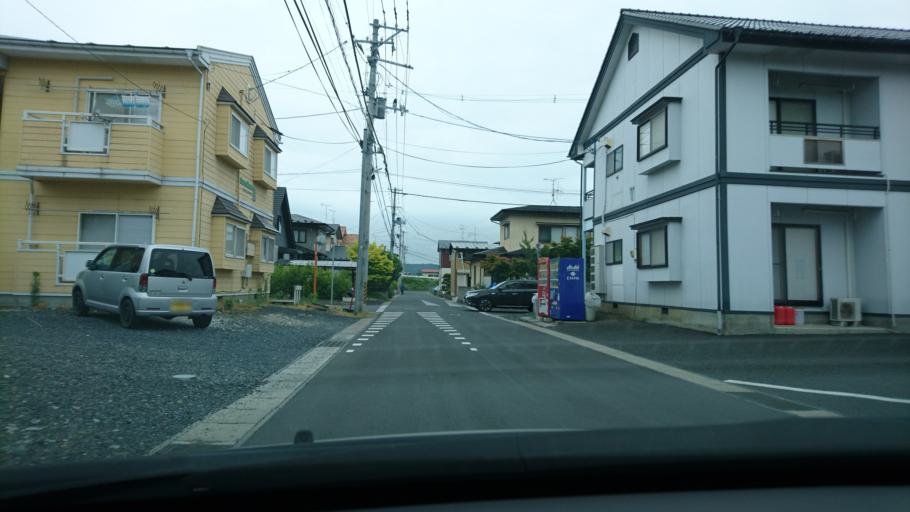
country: JP
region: Iwate
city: Ichinoseki
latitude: 38.9169
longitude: 141.1086
